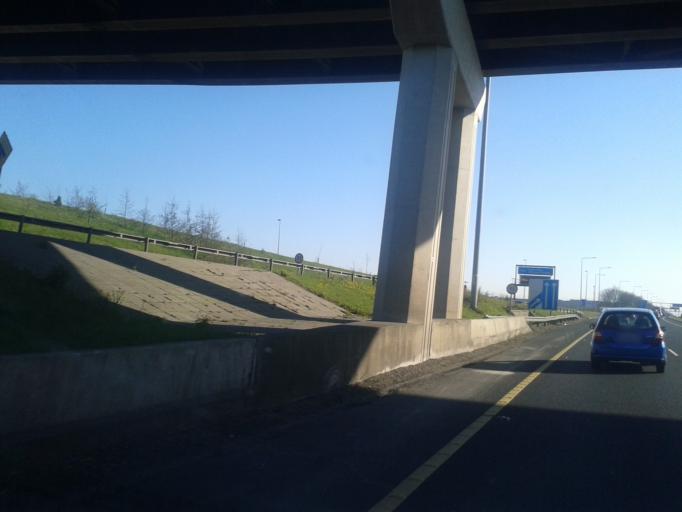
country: IE
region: Leinster
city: Beaumont
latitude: 53.4092
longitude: -6.2272
